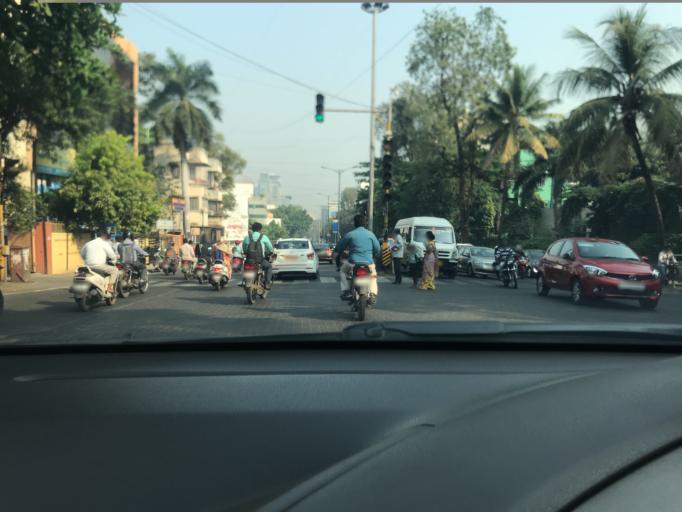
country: IN
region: Maharashtra
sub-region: Pune Division
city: Shivaji Nagar
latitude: 18.5251
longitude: 73.8297
